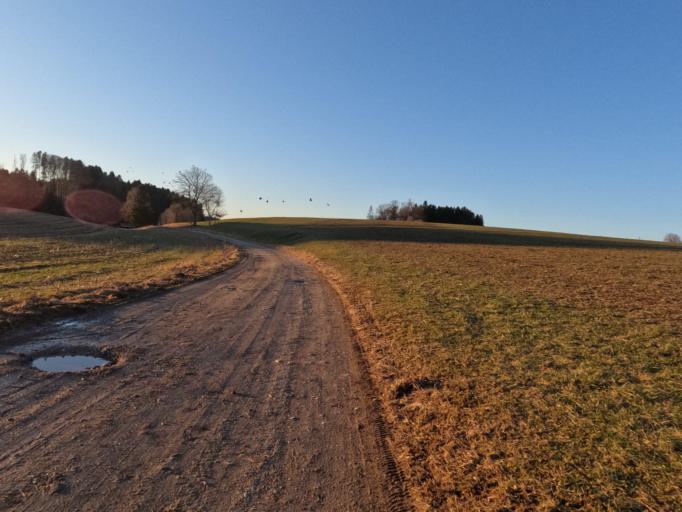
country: DE
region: Bavaria
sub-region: Upper Bavaria
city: Grabenstatt
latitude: 47.8620
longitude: 12.5749
